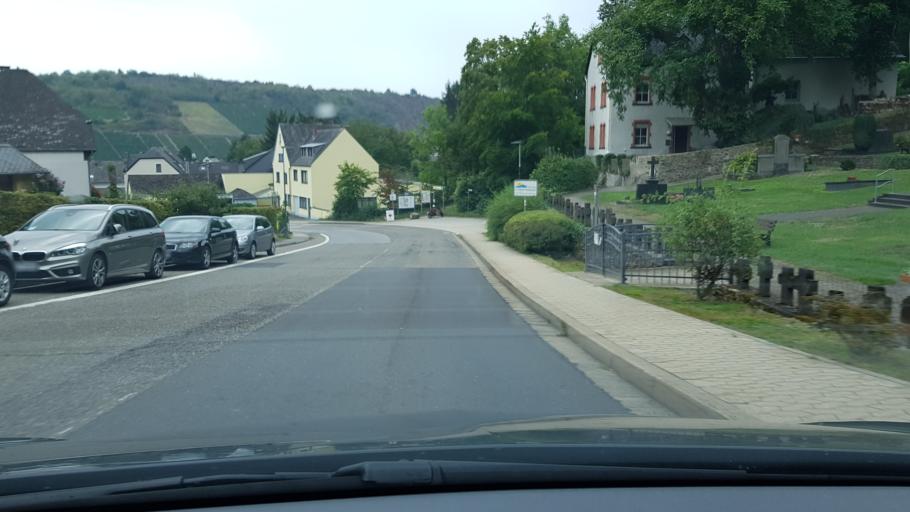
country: DE
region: Rheinland-Pfalz
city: Kobern-Gondorf
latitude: 50.3097
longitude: 7.4547
